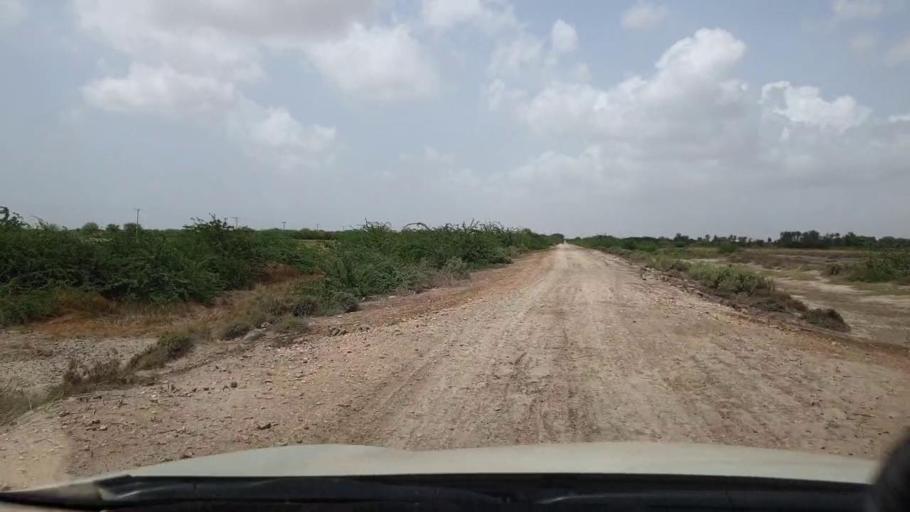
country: PK
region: Sindh
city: Kadhan
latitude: 24.3720
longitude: 68.8550
